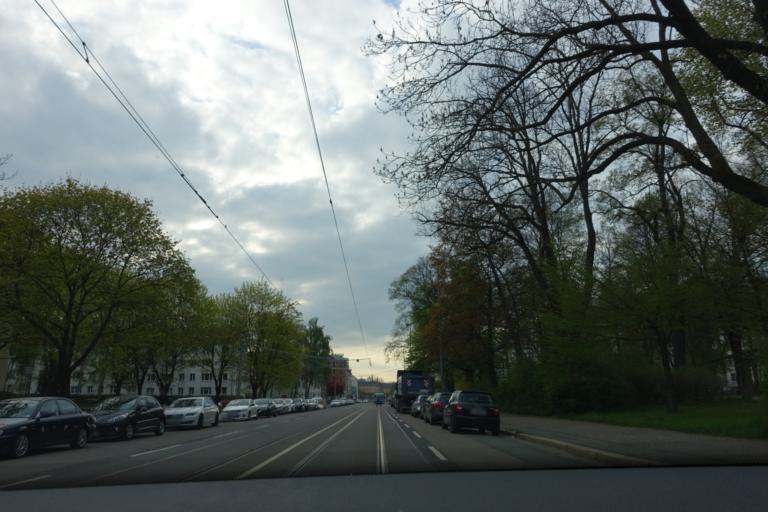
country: DE
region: Saxony
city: Chemnitz
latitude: 50.8212
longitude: 12.9330
